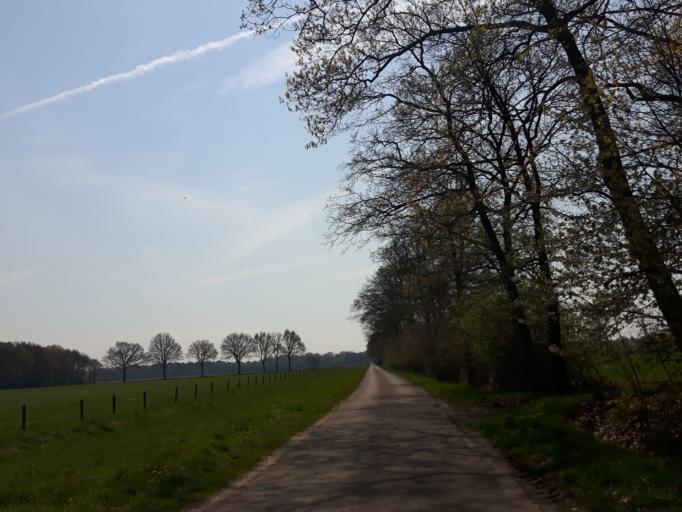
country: DE
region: North Rhine-Westphalia
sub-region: Regierungsbezirk Munster
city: Vreden
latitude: 52.1361
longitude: 6.8392
